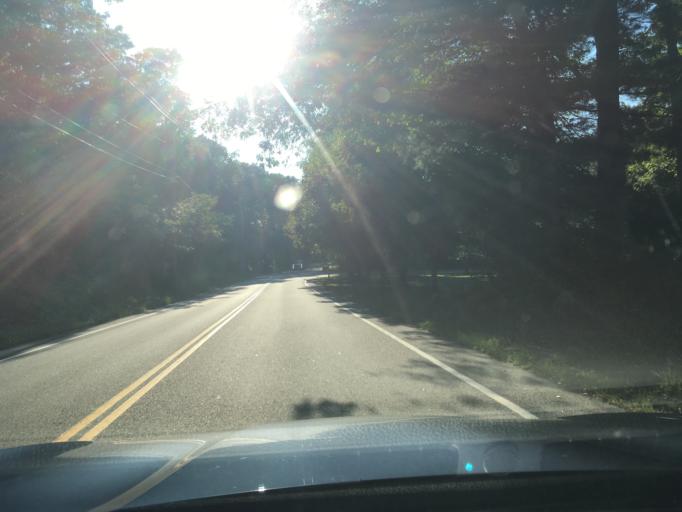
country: US
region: Rhode Island
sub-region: Kent County
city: West Warwick
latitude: 41.6432
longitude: -71.5203
